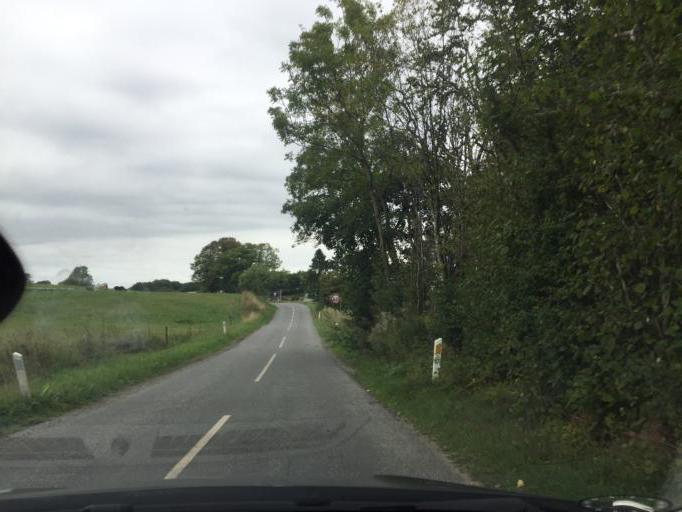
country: DK
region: South Denmark
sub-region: Assens Kommune
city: Arup
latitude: 55.3711
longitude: 10.0855
